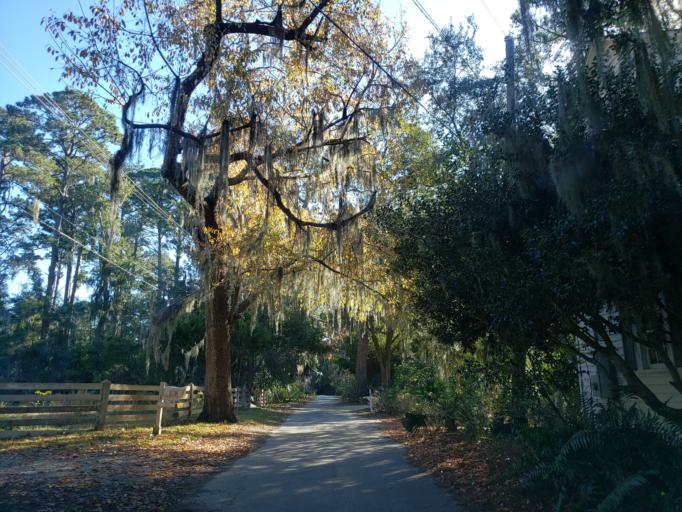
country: US
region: Georgia
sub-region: Chatham County
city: Montgomery
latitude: 31.9658
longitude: -81.1202
